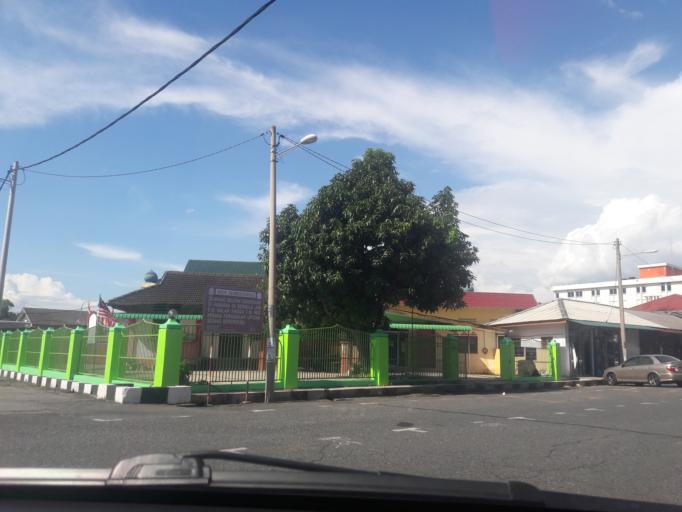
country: MY
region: Kedah
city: Sungai Petani
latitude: 5.6403
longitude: 100.4849
